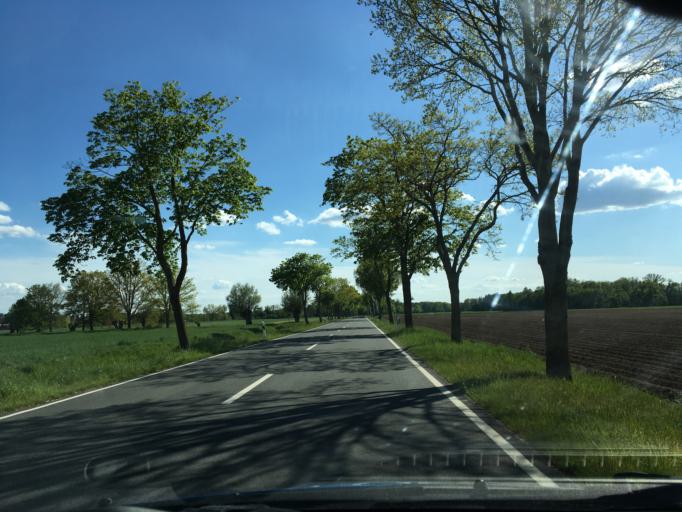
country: DE
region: Brandenburg
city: Lanz
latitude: 53.0250
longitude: 11.5588
